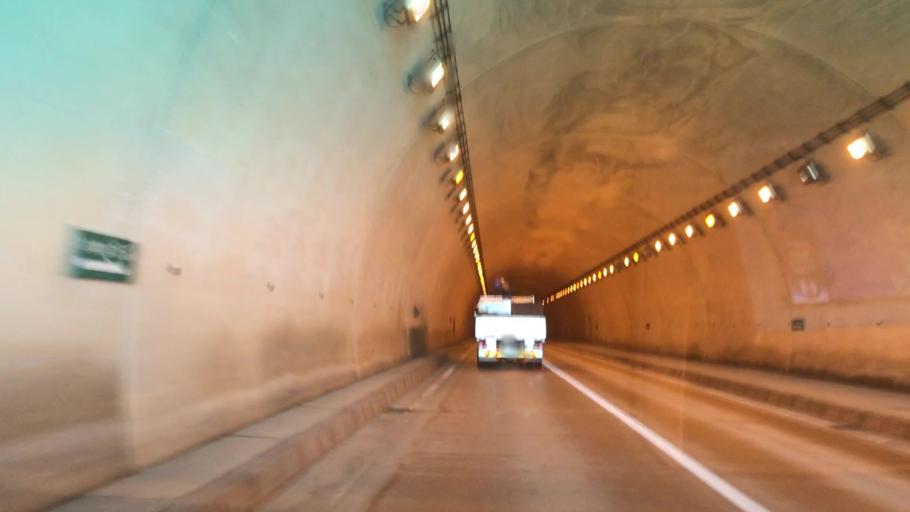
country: JP
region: Hokkaido
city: Iwanai
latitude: 43.1219
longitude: 140.4450
